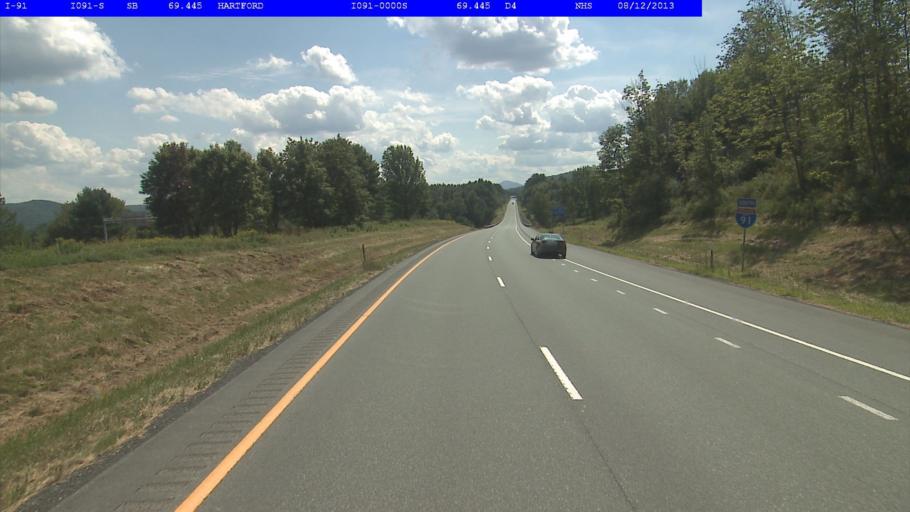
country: US
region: Vermont
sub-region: Windsor County
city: White River Junction
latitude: 43.6347
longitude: -72.3393
